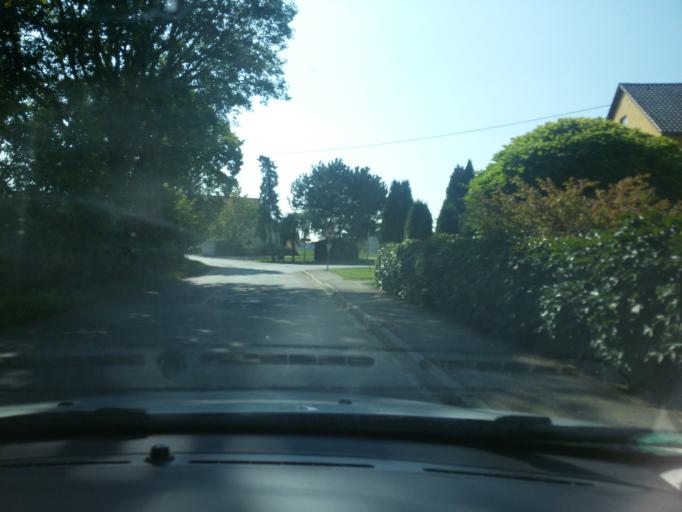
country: DE
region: Bavaria
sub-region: Swabia
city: Hiltenfingen
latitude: 48.1848
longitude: 10.6814
